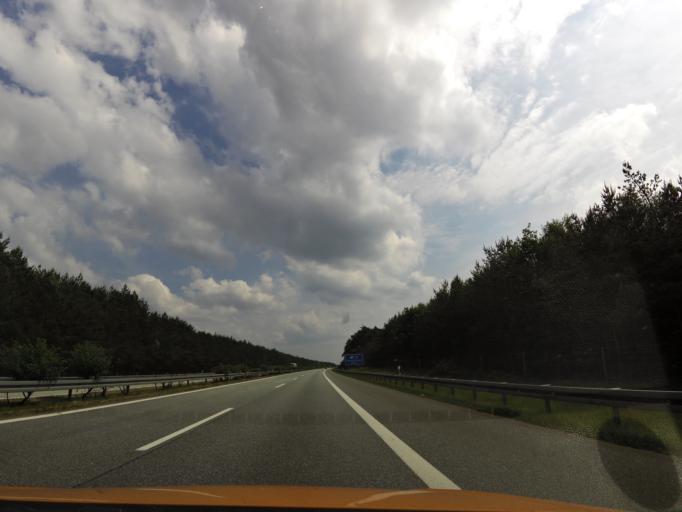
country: DE
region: Mecklenburg-Vorpommern
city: Neustadt-Glewe
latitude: 53.3895
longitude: 11.6057
